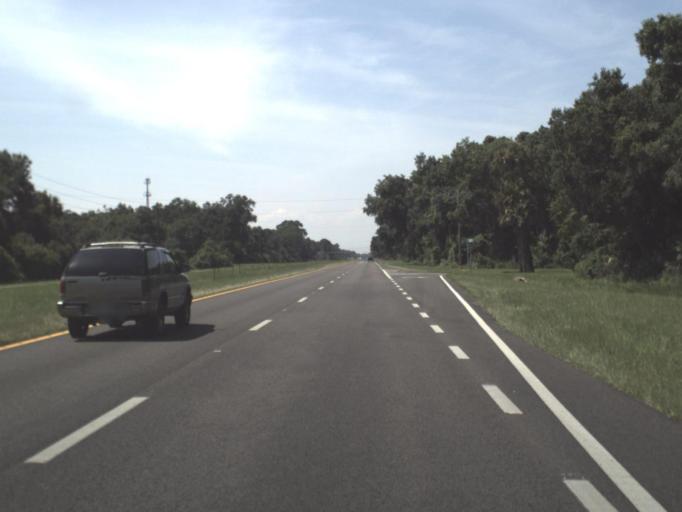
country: US
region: Florida
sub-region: Citrus County
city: Crystal River
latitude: 28.9439
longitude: -82.6224
